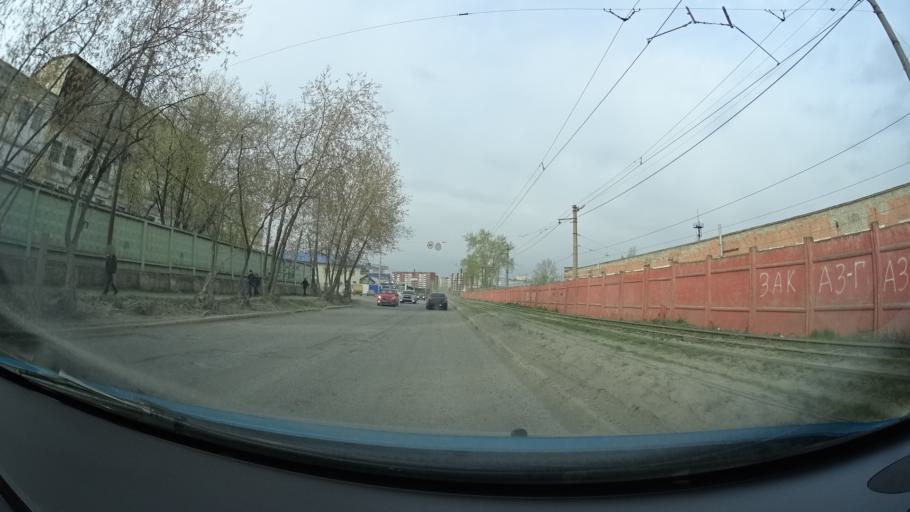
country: RU
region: Perm
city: Kondratovo
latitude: 58.0030
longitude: 56.1523
